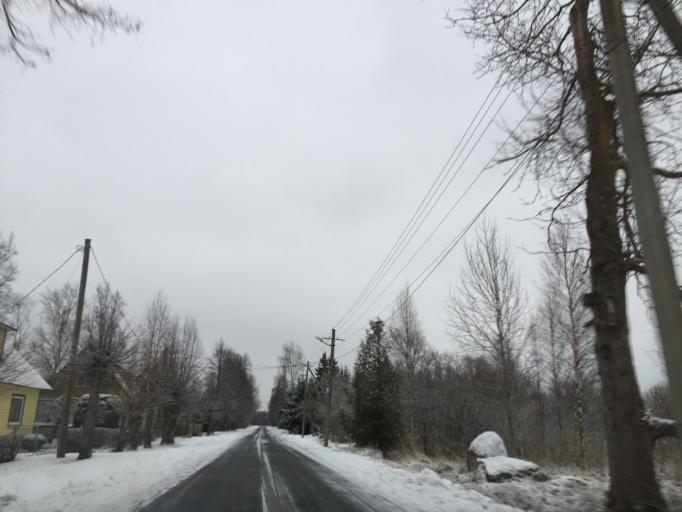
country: EE
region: Laeaene
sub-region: Lihula vald
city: Lihula
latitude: 58.6828
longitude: 23.8342
